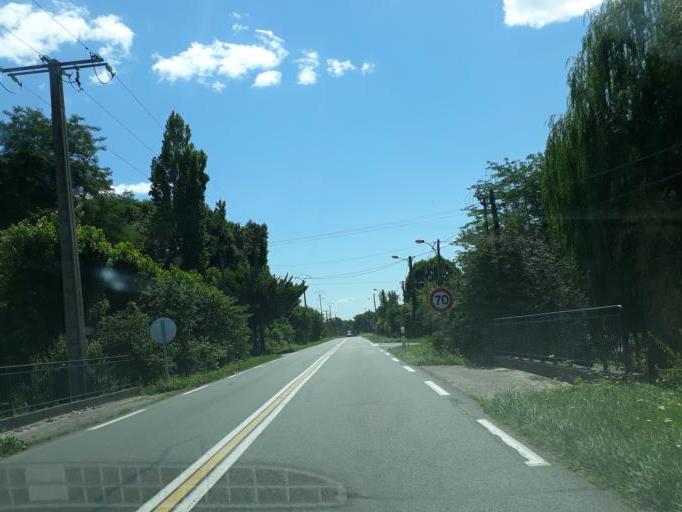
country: FR
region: Centre
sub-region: Departement du Loiret
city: Bray-en-Val
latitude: 47.8047
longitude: 2.3810
